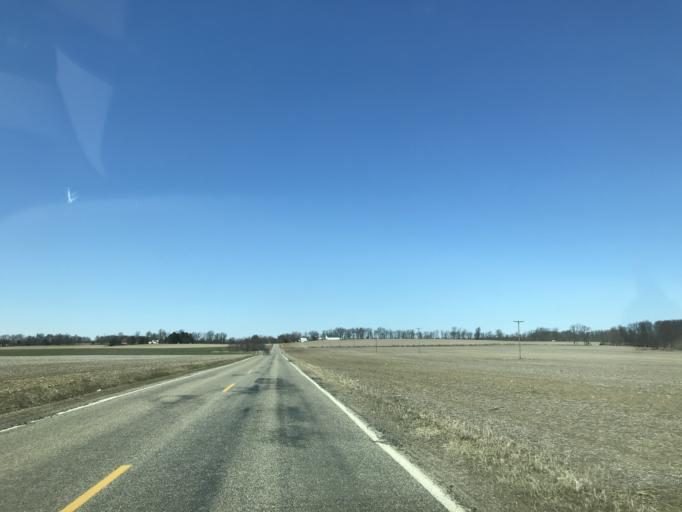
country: US
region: Michigan
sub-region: Hillsdale County
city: Jonesville
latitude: 41.9855
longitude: -84.7165
